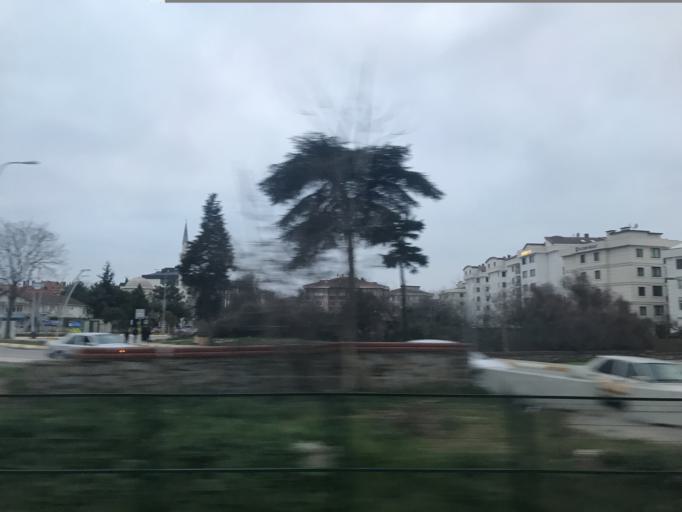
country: TR
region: Istanbul
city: Icmeler
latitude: 40.8275
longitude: 29.3254
